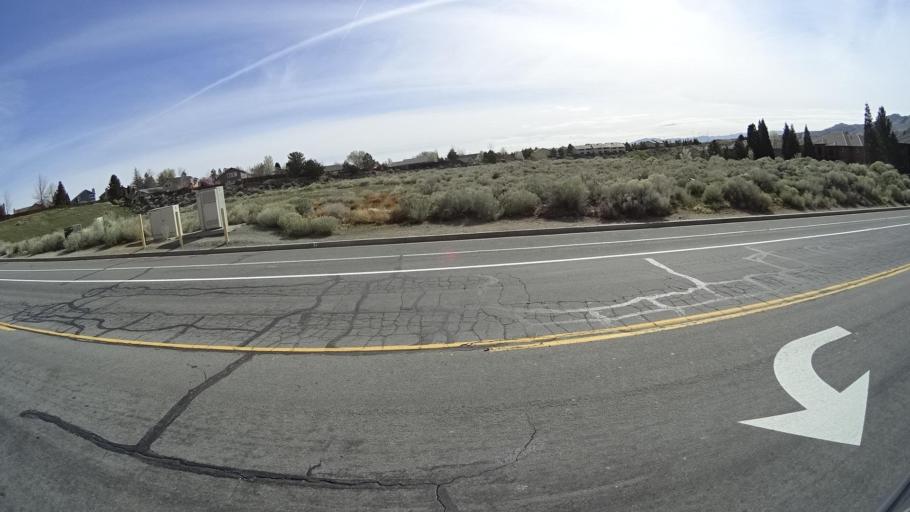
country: US
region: Nevada
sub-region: Washoe County
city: Mogul
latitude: 39.5200
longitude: -119.8974
